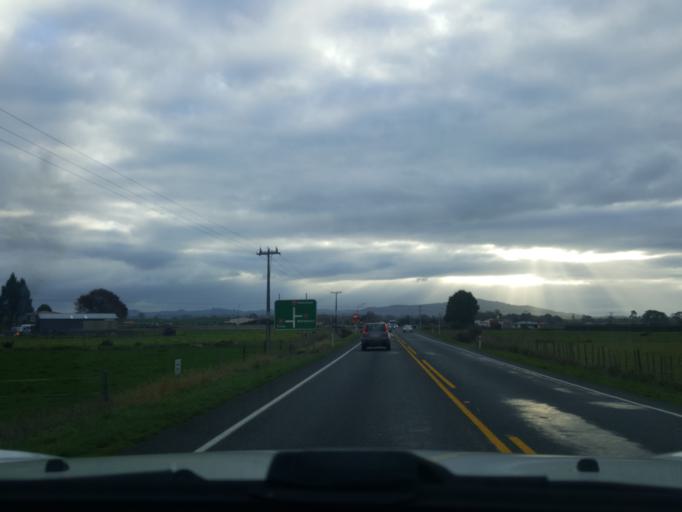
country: NZ
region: Waikato
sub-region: Matamata-Piako District
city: Matamata
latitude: -37.8896
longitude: 175.7790
